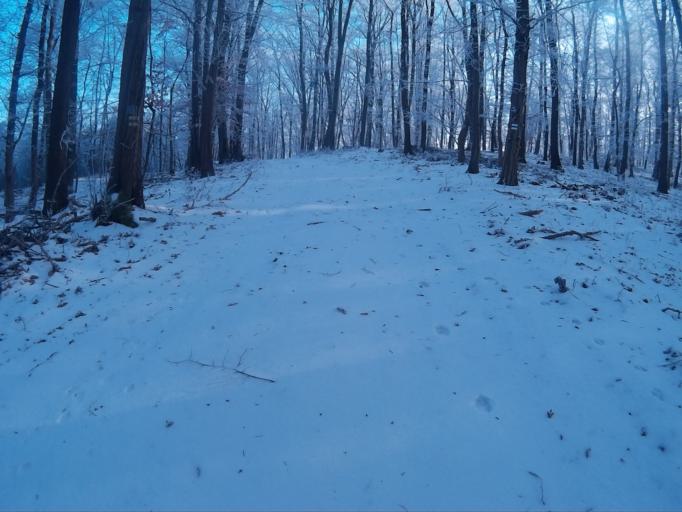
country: HU
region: Borsod-Abauj-Zemplen
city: Szendro
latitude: 48.4916
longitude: 20.7447
